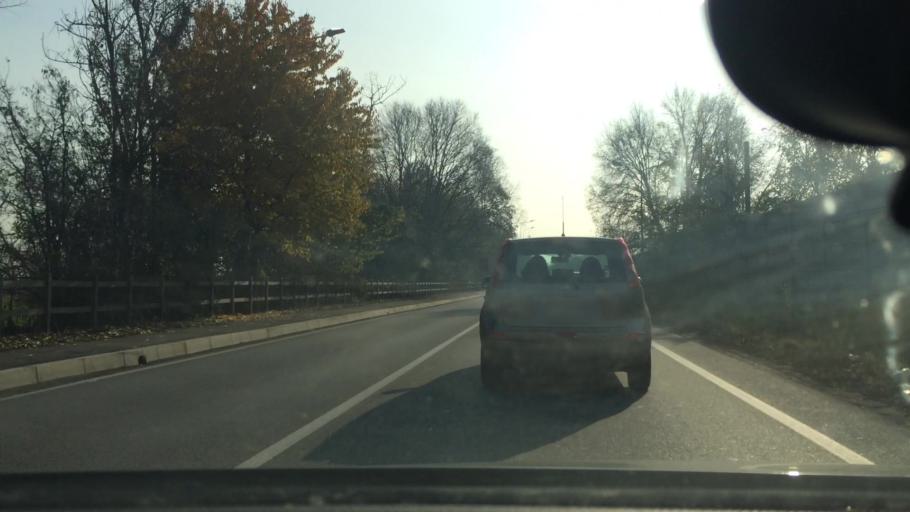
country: IT
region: Lombardy
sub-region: Citta metropolitana di Milano
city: Passirana
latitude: 45.5591
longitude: 9.0522
